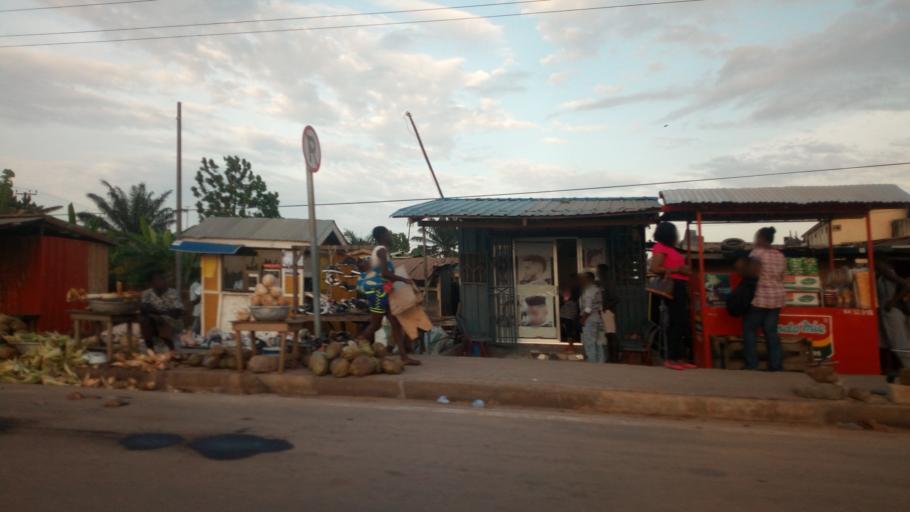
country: GH
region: Western
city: Takoradi
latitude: 4.9328
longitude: -1.7793
